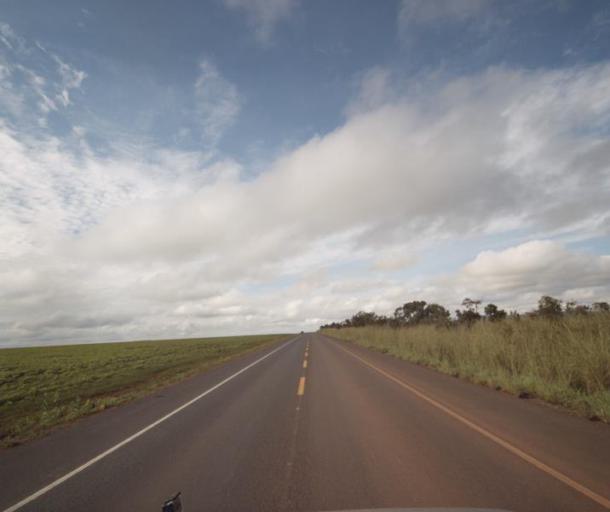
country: BR
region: Goias
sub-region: Padre Bernardo
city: Padre Bernardo
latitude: -15.4245
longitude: -48.6226
